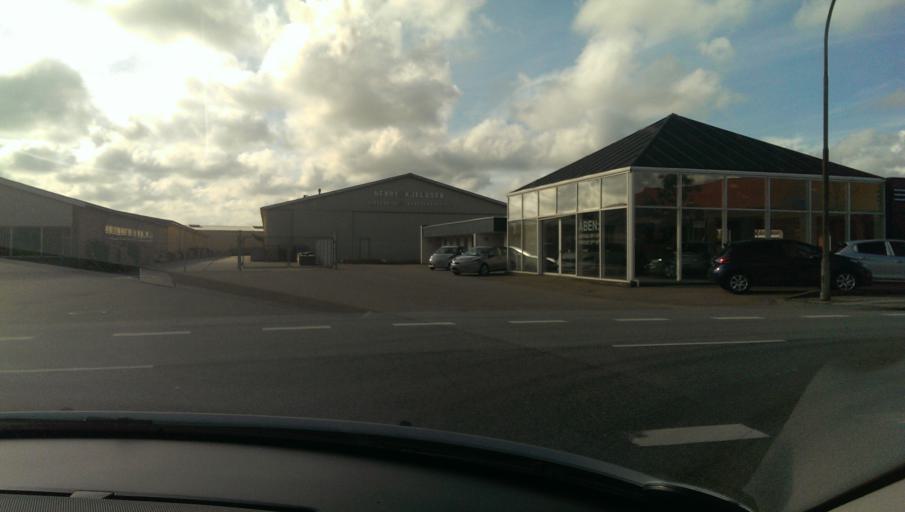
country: DK
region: Central Jutland
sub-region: Ringkobing-Skjern Kommune
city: Ringkobing
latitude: 56.0925
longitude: 8.2427
